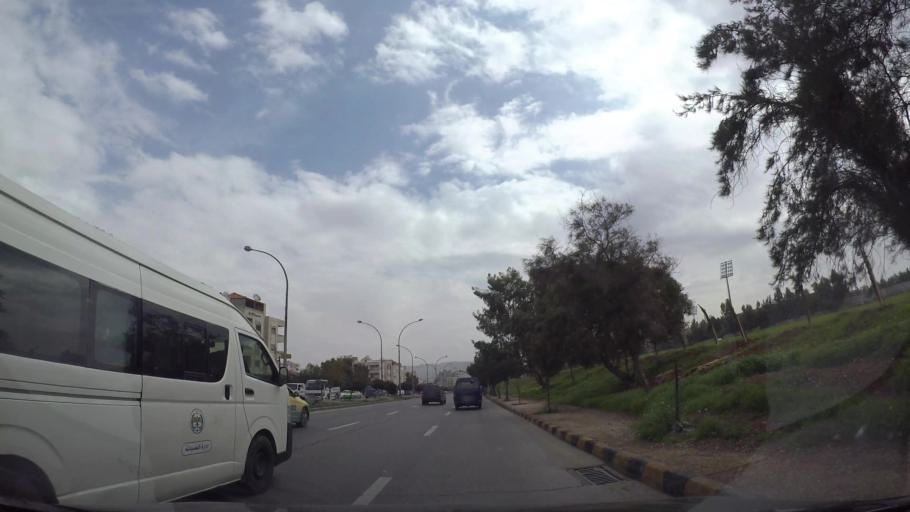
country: JO
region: Amman
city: Amman
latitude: 31.9703
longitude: 35.9411
